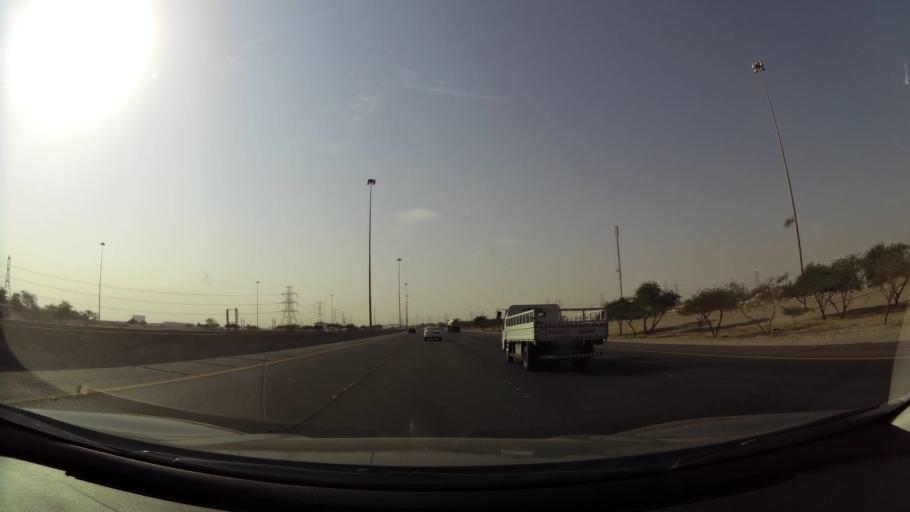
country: KW
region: Al Ahmadi
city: Al Ahmadi
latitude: 29.0293
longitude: 48.0917
